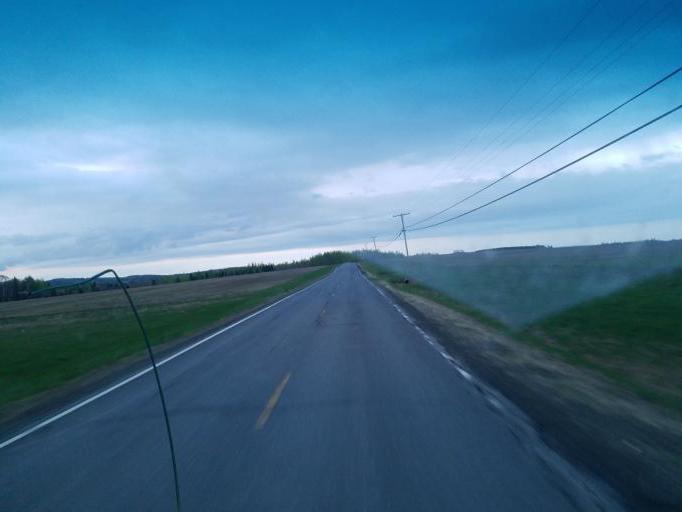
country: US
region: Maine
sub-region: Aroostook County
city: Caribou
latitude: 46.8262
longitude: -68.1733
